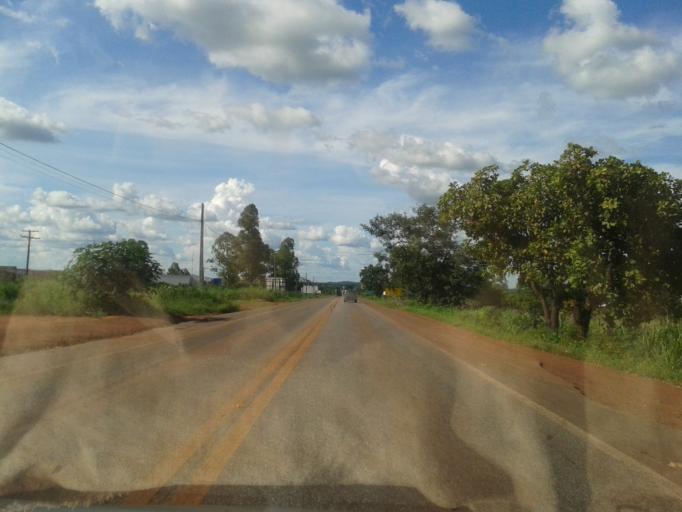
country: BR
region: Goias
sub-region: Mozarlandia
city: Mozarlandia
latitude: -14.7618
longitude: -50.5389
